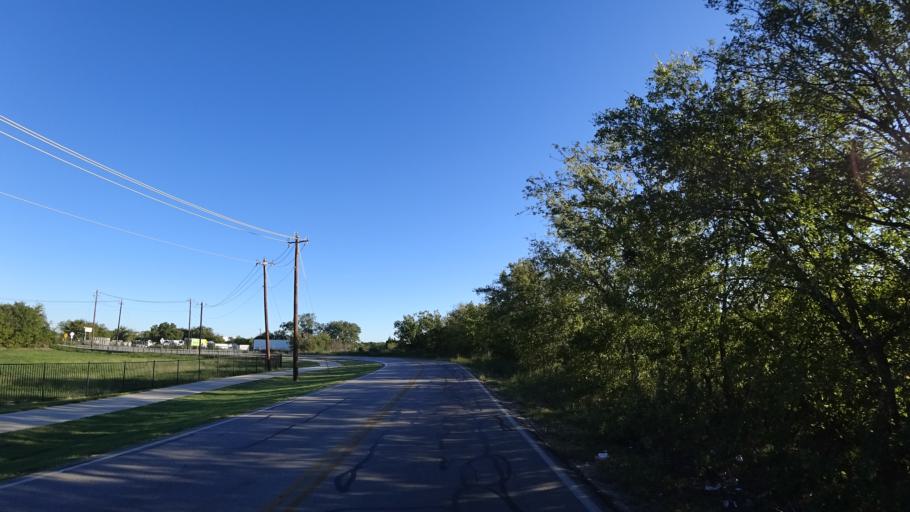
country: US
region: Texas
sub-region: Travis County
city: Manor
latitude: 30.3188
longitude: -97.6261
